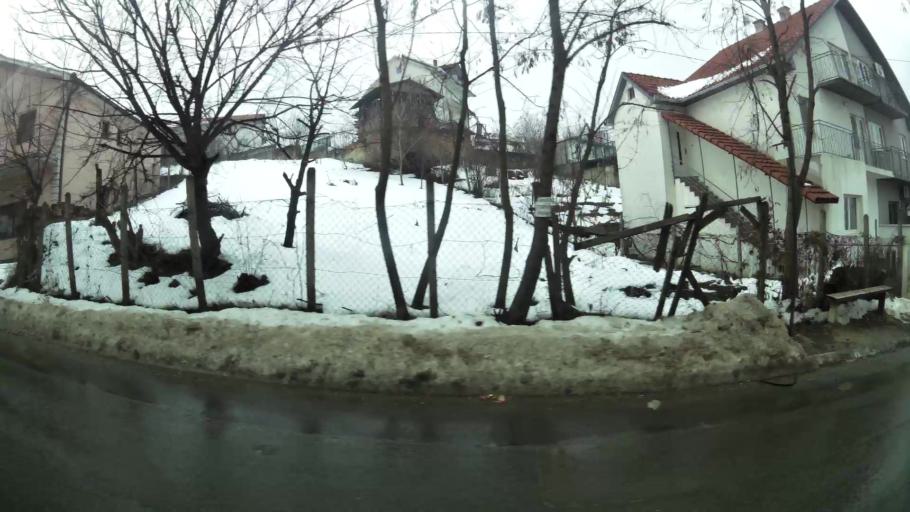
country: RS
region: Central Serbia
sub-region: Belgrade
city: Zvezdara
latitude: 44.7623
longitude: 20.5259
